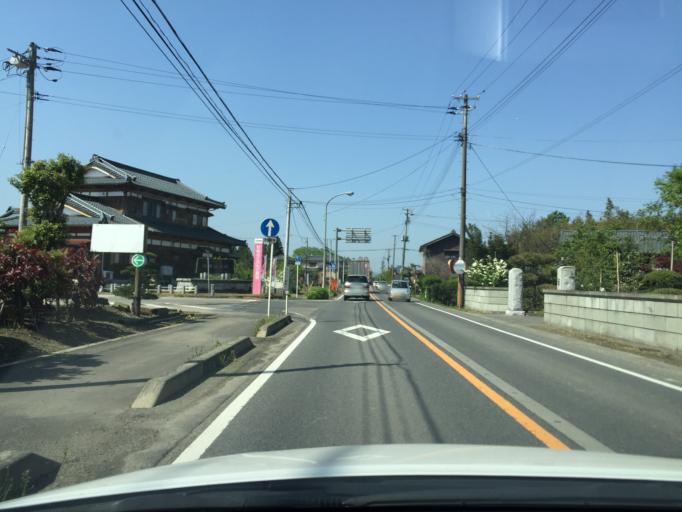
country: JP
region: Niigata
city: Muramatsu
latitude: 37.7076
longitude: 139.2025
